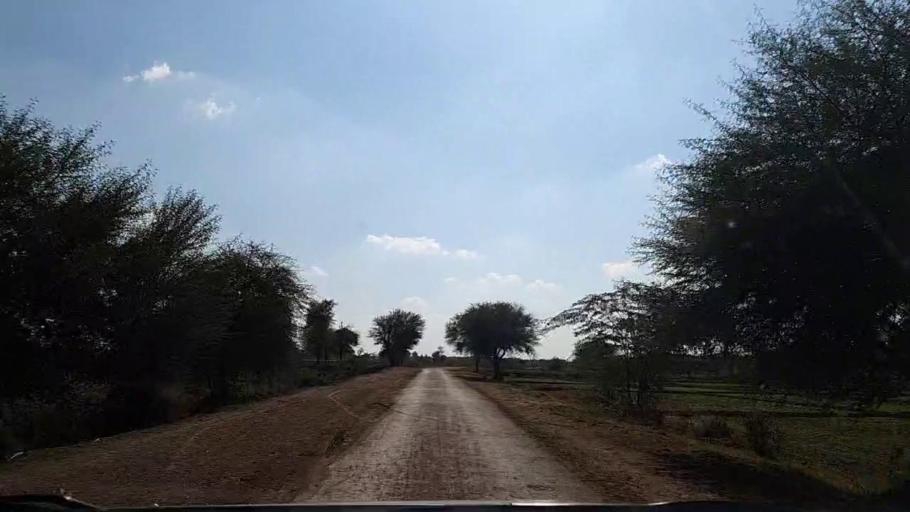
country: PK
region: Sindh
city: Pithoro
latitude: 25.6496
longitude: 69.4484
